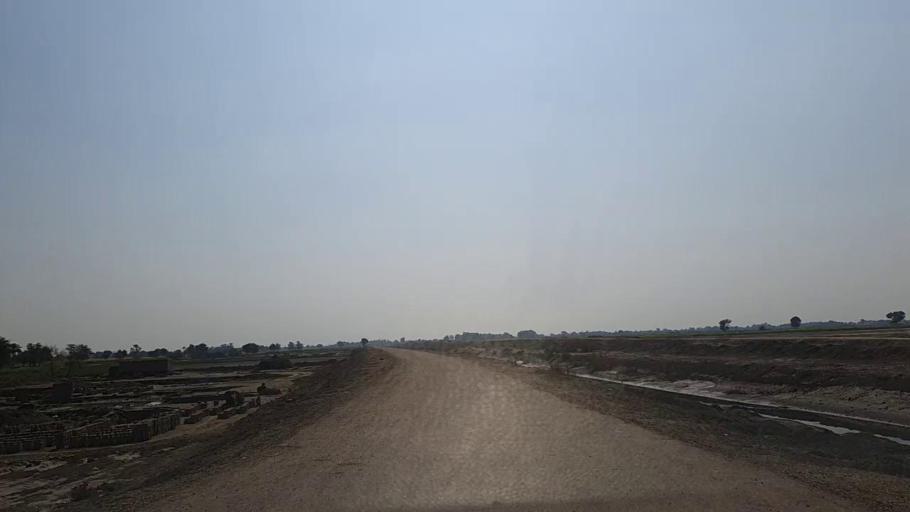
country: PK
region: Sindh
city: Nawabshah
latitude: 26.2644
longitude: 68.5031
